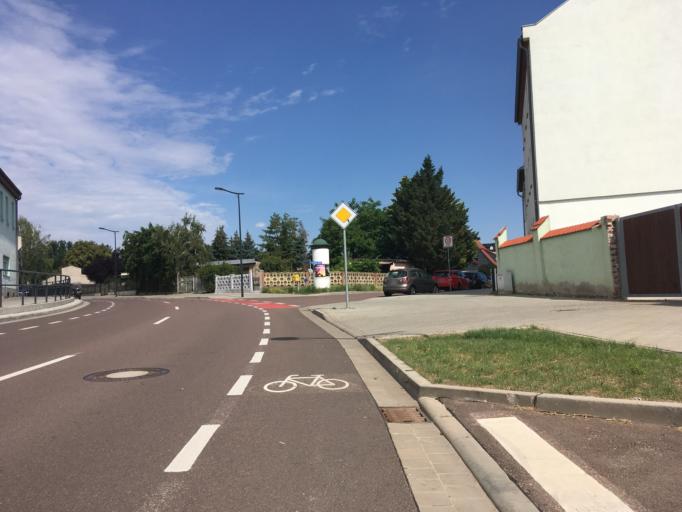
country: DE
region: Saxony-Anhalt
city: Bernburg
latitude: 51.7813
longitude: 11.7664
